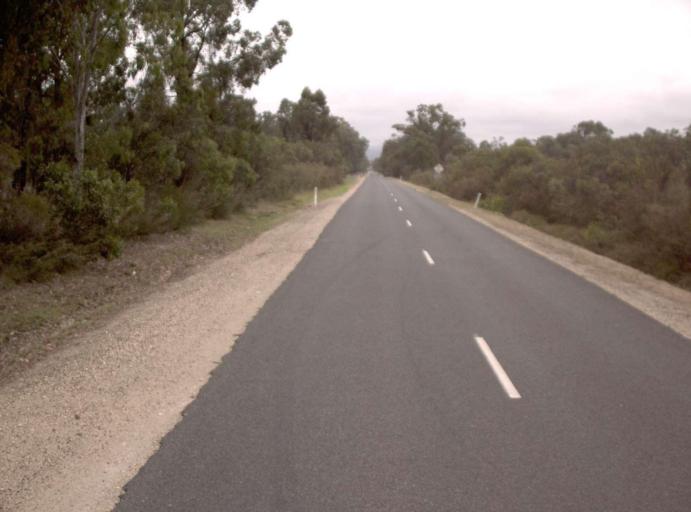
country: AU
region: Victoria
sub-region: Wellington
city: Heyfield
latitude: -37.9281
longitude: 146.7551
